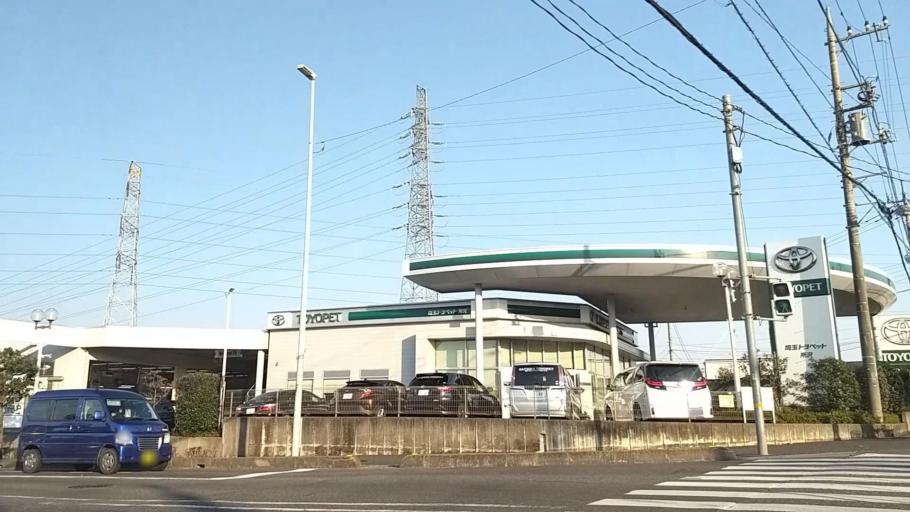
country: JP
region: Saitama
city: Tokorozawa
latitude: 35.7925
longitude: 139.4431
